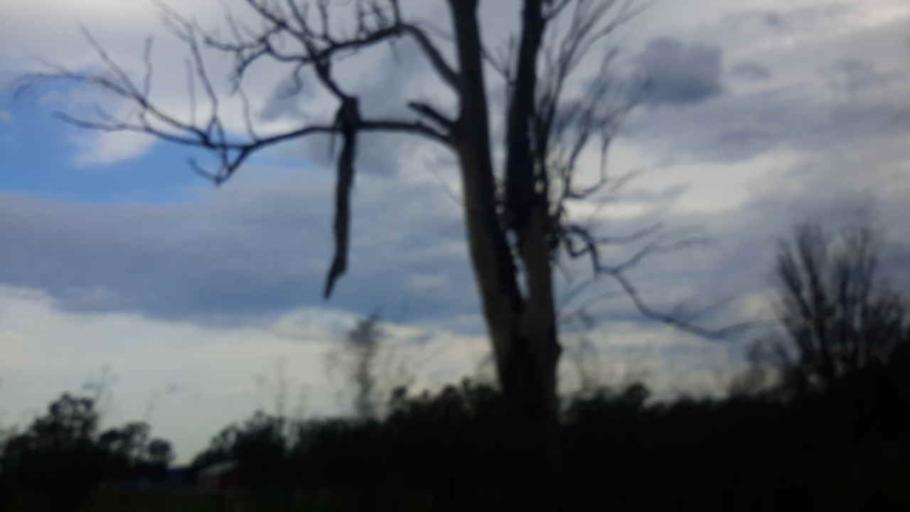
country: AU
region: New South Wales
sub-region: Penrith Municipality
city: Glenmore Park
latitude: -33.8202
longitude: 150.6860
